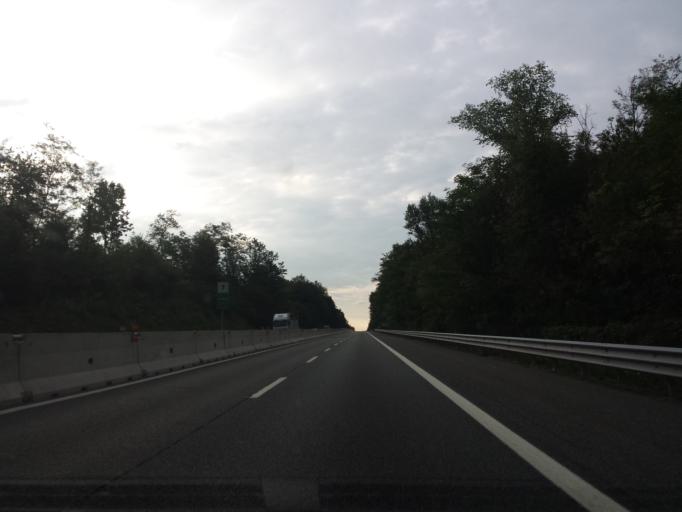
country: IT
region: Lombardy
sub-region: Provincia di Varese
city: Arsago Seprio
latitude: 45.7075
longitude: 8.7256
